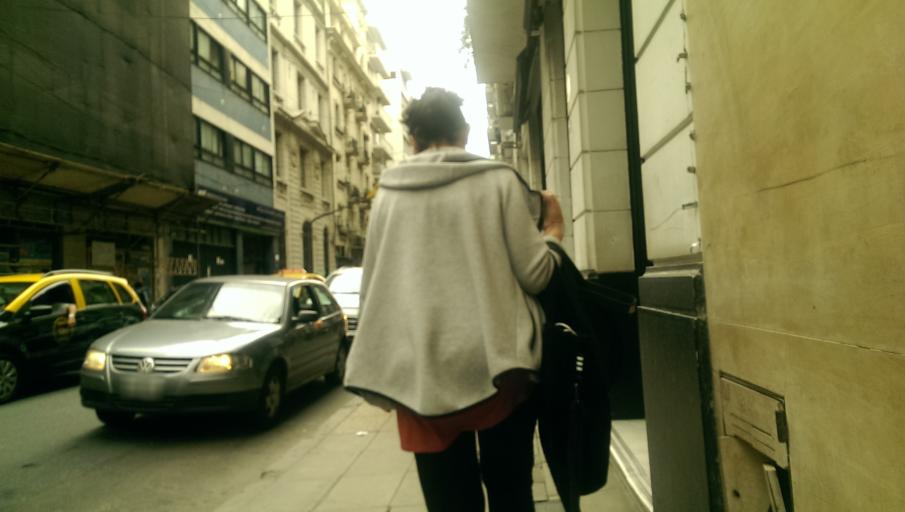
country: AR
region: Buenos Aires F.D.
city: Retiro
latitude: -34.5983
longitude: -58.3868
